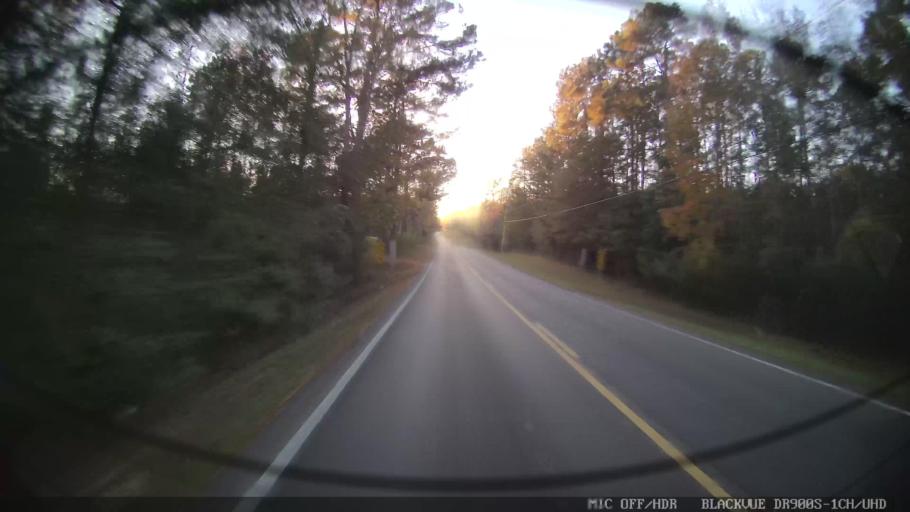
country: US
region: Mississippi
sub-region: Stone County
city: Wiggins
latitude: 31.0320
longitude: -89.2247
